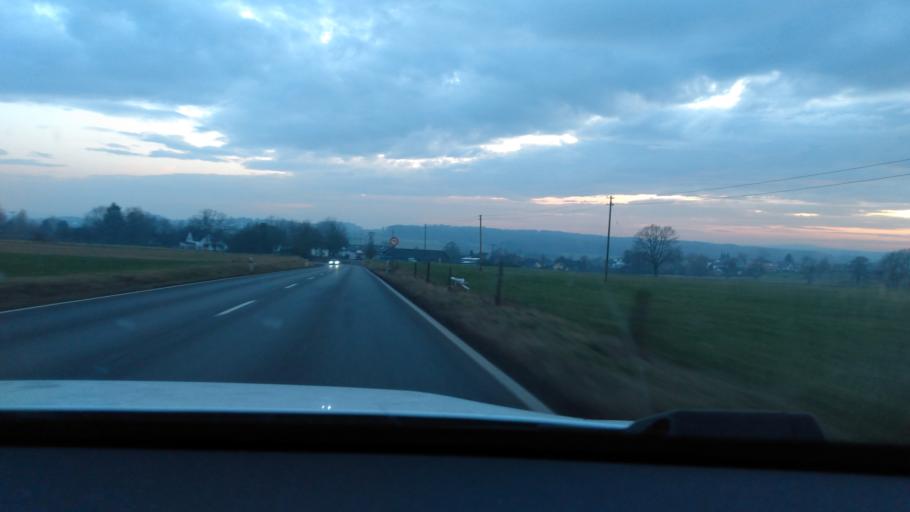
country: DE
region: Rheinland-Pfalz
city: Kircheib
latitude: 50.7040
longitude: 7.4358
